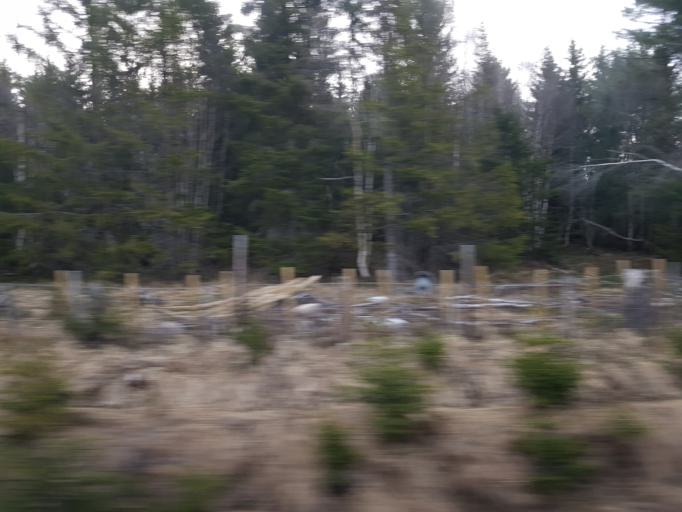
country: NO
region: Sor-Trondelag
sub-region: Rennebu
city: Berkak
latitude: 62.8545
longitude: 10.0236
